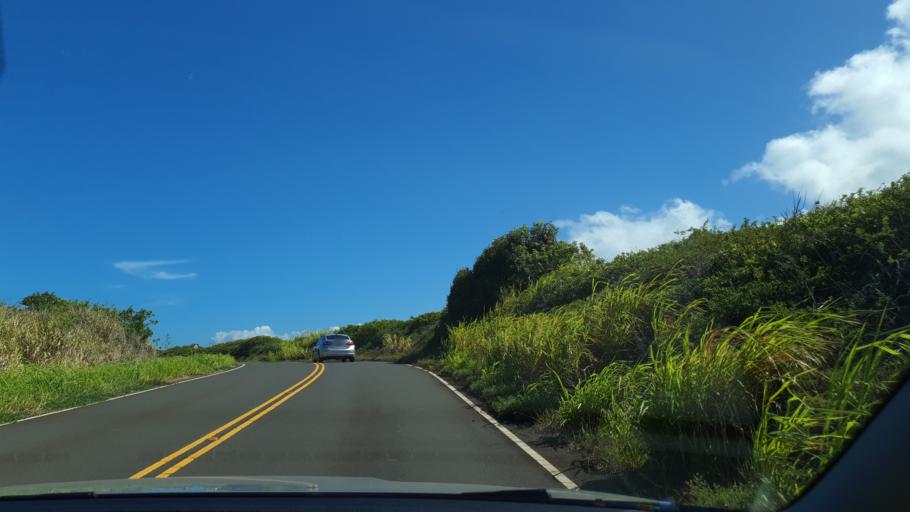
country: US
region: Hawaii
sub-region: Maui County
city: Napili-Honokowai
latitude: 21.0148
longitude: -156.5740
